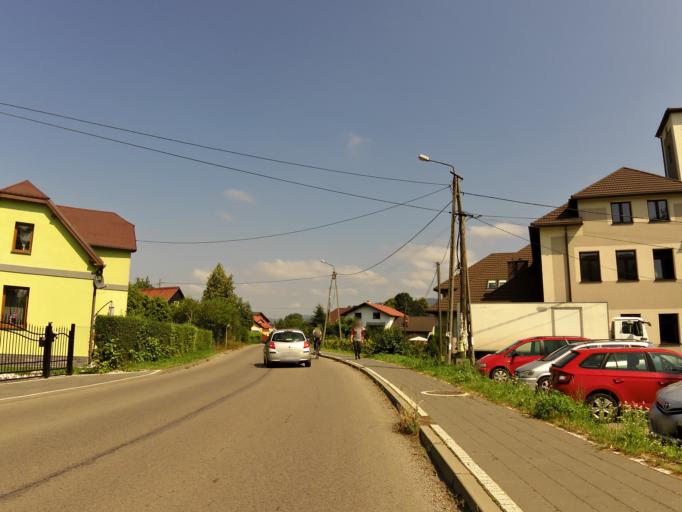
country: PL
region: Silesian Voivodeship
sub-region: Powiat zywiecki
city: Ciecina
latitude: 49.6168
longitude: 19.1352
